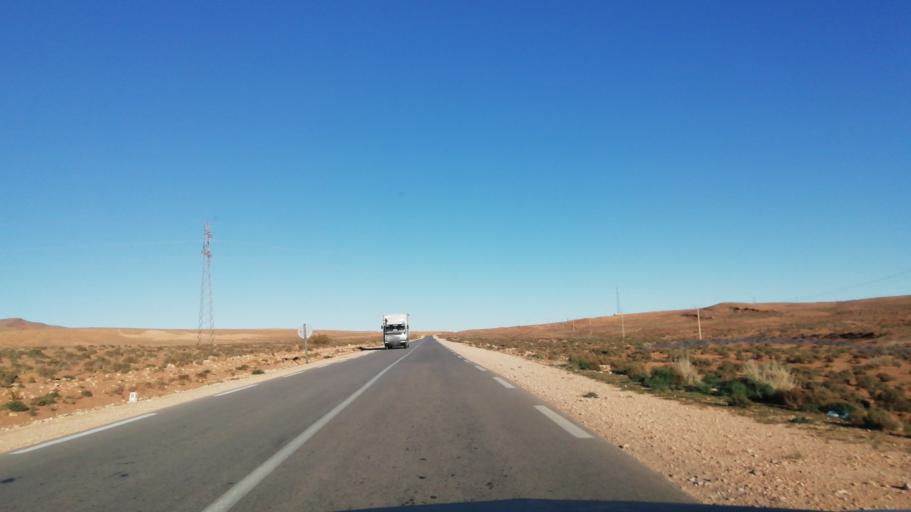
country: DZ
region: El Bayadh
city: El Abiodh Sidi Cheikh
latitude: 33.1698
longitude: 0.4326
